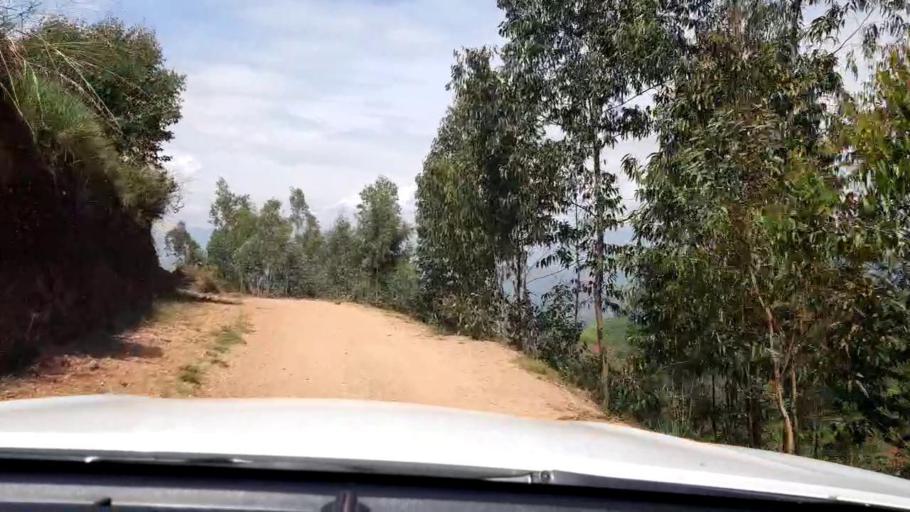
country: RW
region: Southern Province
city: Gitarama
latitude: -2.0554
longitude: 29.6712
